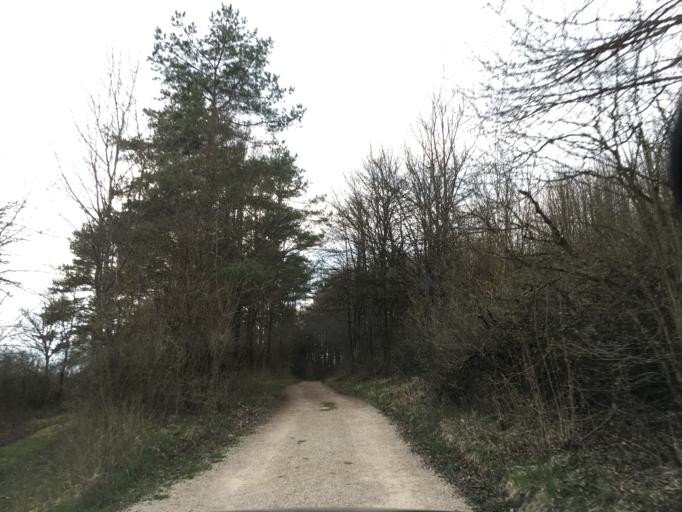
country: DE
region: Bavaria
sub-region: Upper Franconia
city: Pottenstein
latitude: 49.7614
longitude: 11.4318
